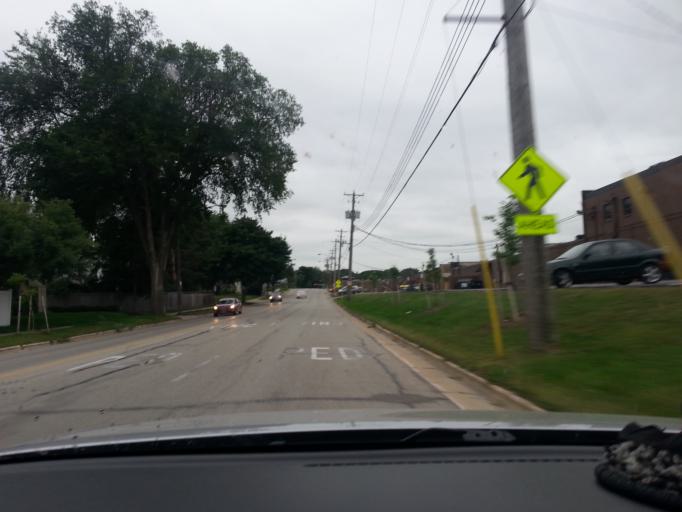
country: US
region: Minnesota
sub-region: Olmsted County
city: Rochester
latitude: 44.0253
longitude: -92.4861
